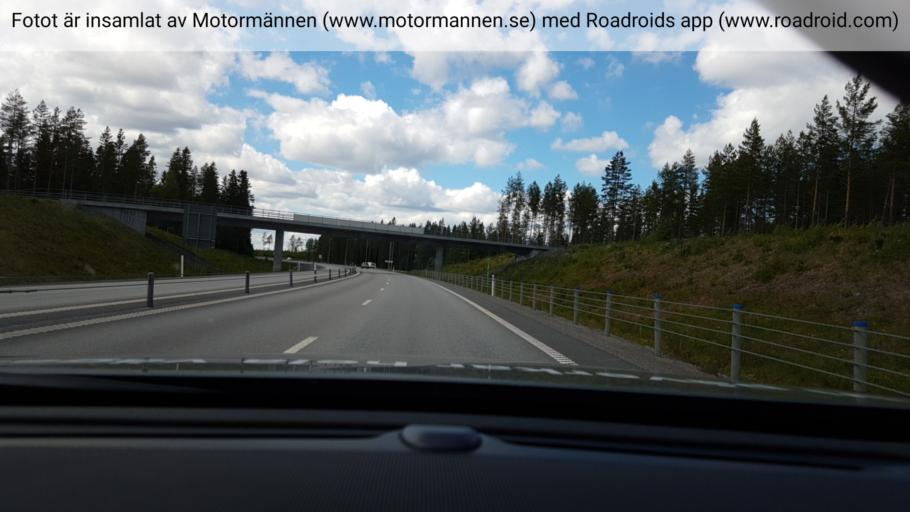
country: SE
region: Vaesterbotten
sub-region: Umea Kommun
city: Umea
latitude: 63.8523
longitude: 20.2886
